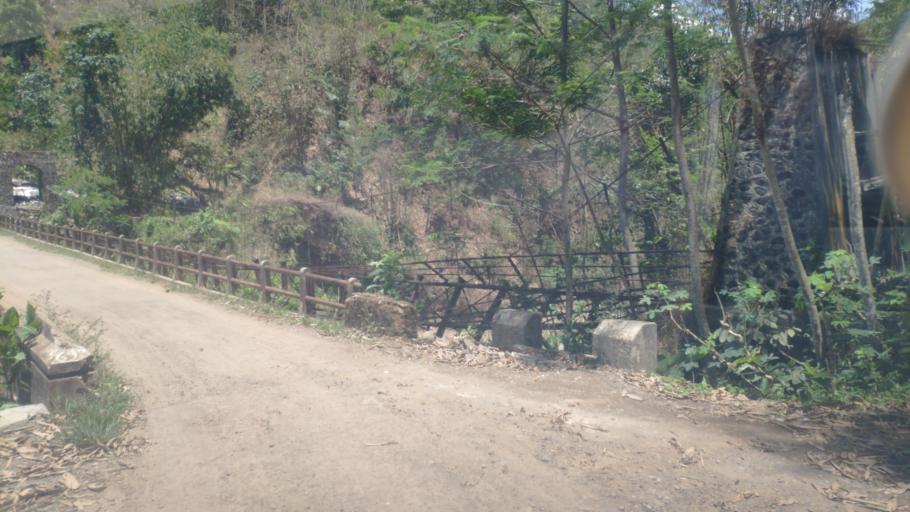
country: ID
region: Central Java
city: Buaran
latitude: -7.2724
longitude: 109.5948
